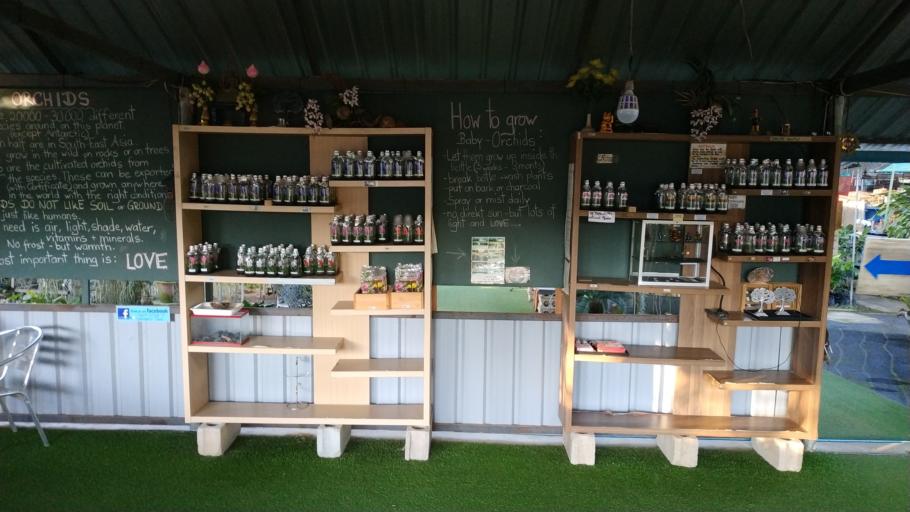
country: TH
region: Phuket
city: Ban Chalong
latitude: 7.8182
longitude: 98.3344
